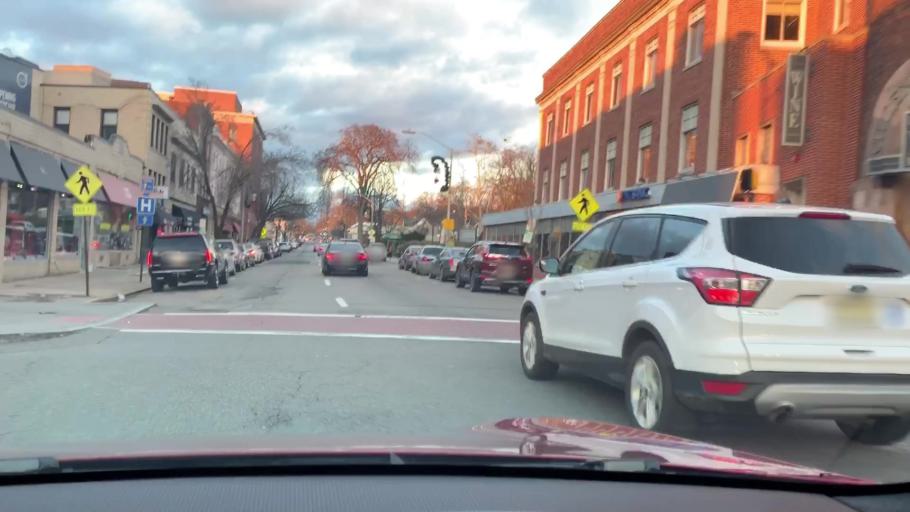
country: US
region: New Jersey
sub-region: Bergen County
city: Englewood
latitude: 40.8929
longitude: -73.9731
